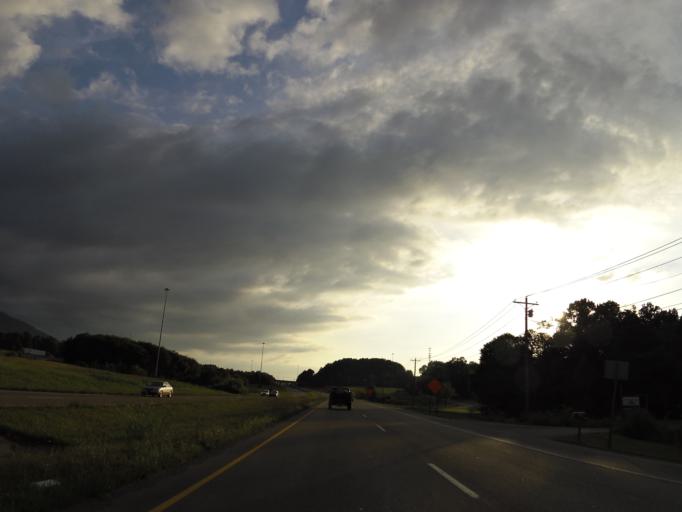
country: US
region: Tennessee
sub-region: Cocke County
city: Newport
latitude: 35.9717
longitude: -83.2493
